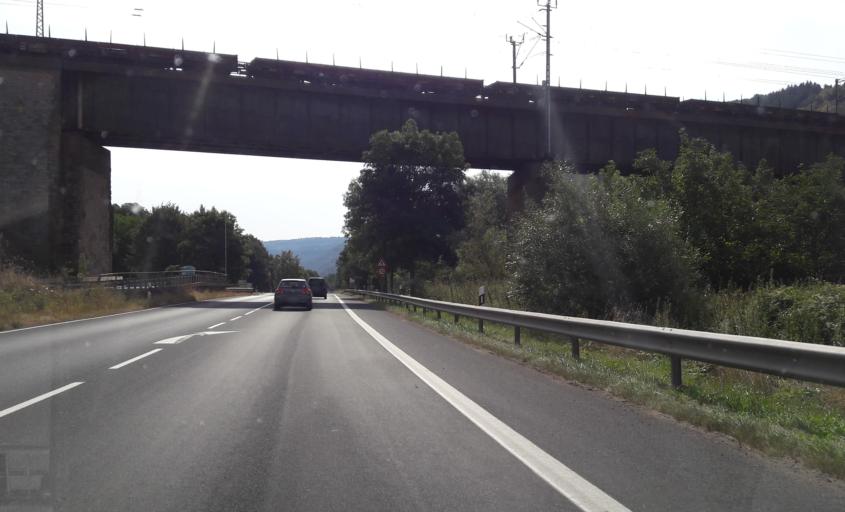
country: DE
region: Rheinland-Pfalz
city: Neef
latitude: 50.1028
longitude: 7.1376
